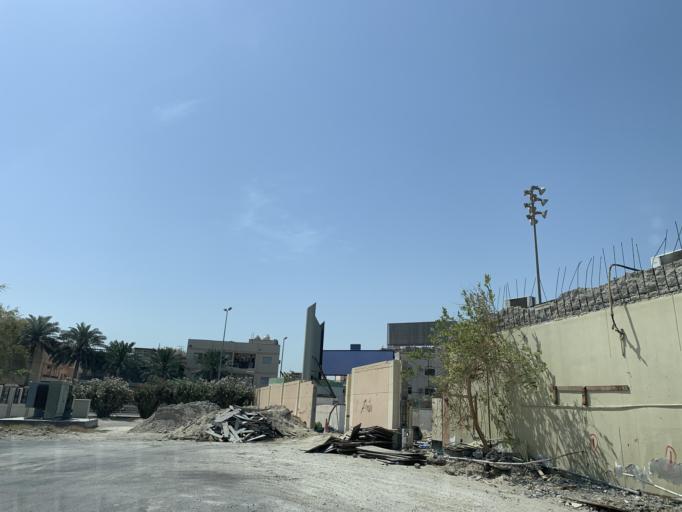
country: BH
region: Muharraq
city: Al Muharraq
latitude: 26.2637
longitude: 50.6142
